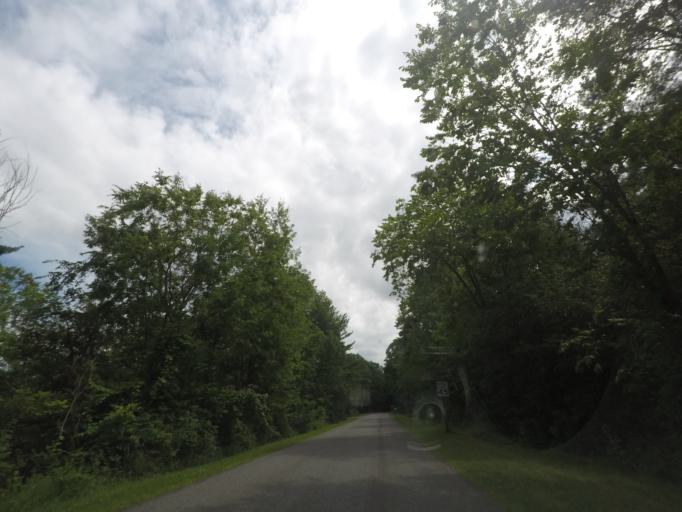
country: US
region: New York
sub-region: Saratoga County
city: Stillwater
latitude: 43.0142
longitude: -73.6458
